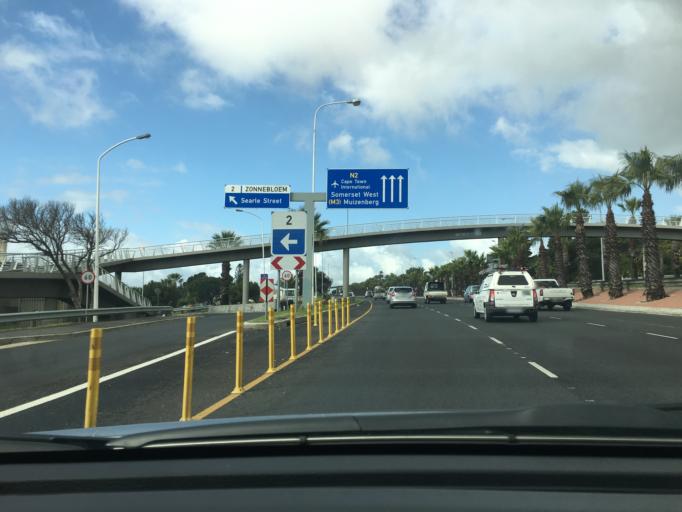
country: ZA
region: Western Cape
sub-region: City of Cape Town
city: Cape Town
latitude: -33.9317
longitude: 18.4397
